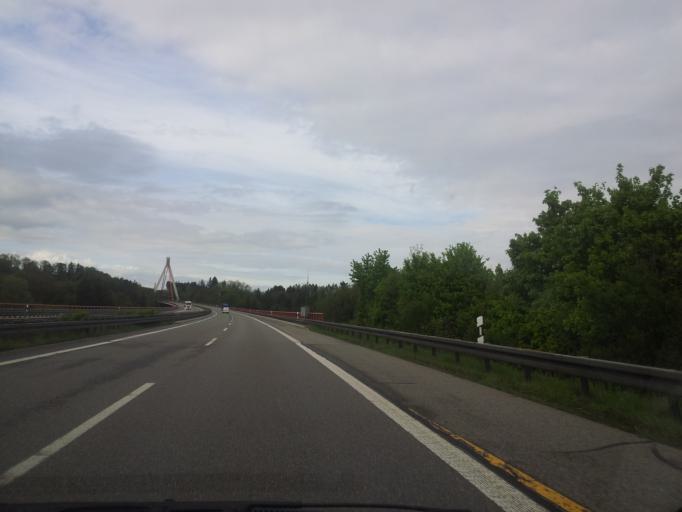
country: DE
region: Bavaria
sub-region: Swabia
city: Hergensweiler
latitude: 47.6464
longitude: 9.7510
